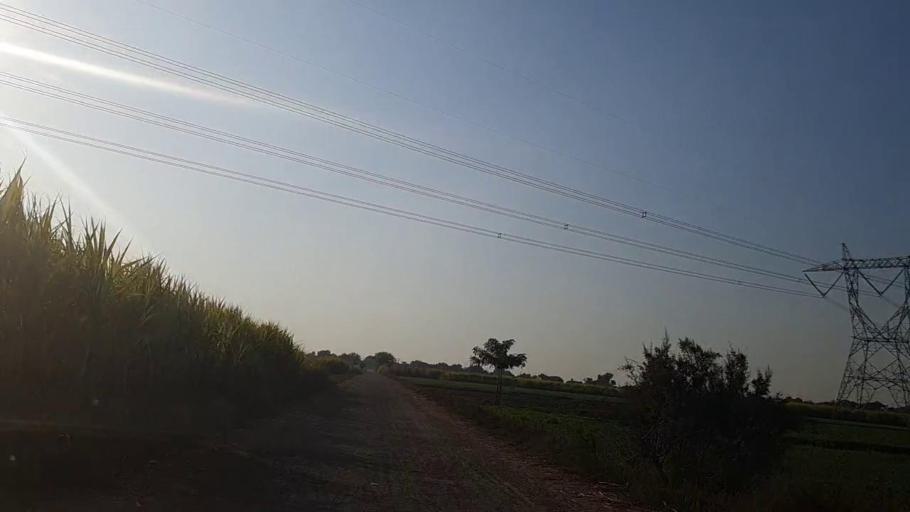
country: PK
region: Sindh
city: Sakrand
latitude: 26.3110
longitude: 68.1484
